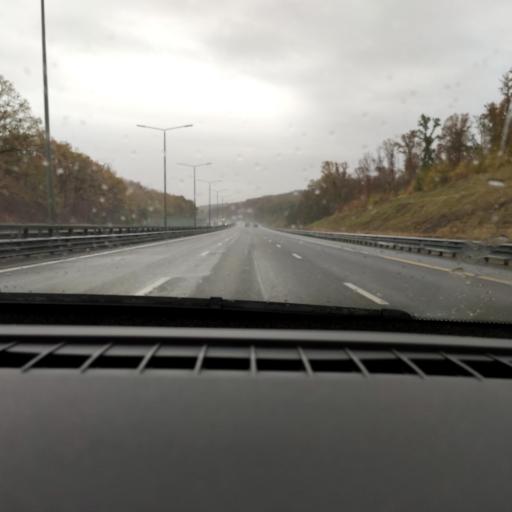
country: RU
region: Voronezj
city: Podgornoye
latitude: 51.8049
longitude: 39.2538
